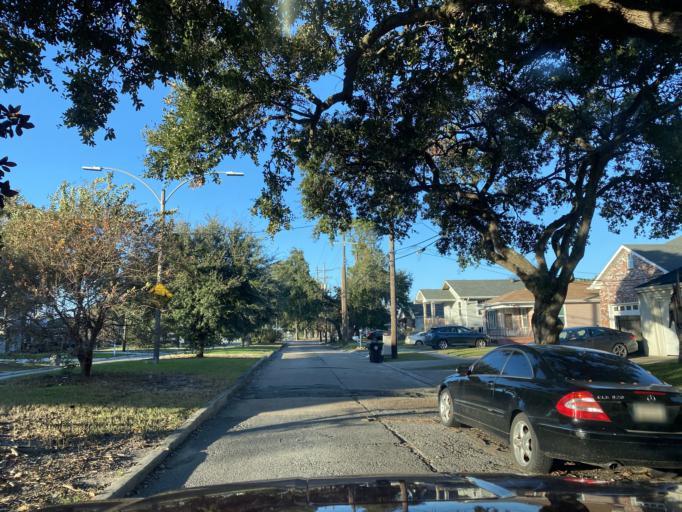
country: US
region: Louisiana
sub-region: Orleans Parish
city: New Orleans
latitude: 30.0121
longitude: -90.0557
